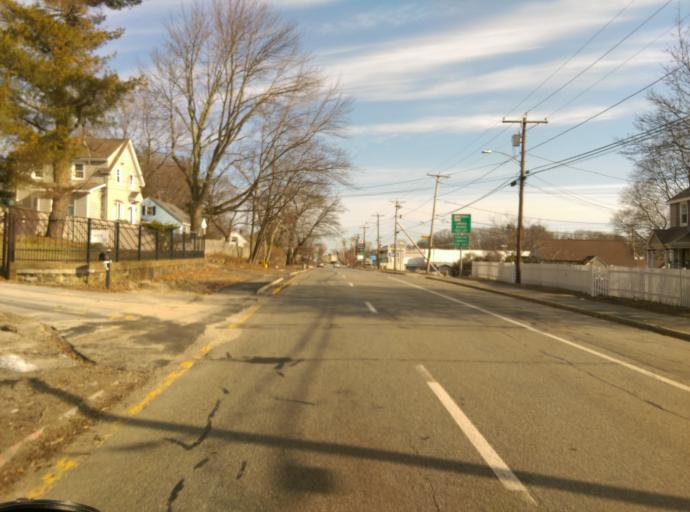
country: US
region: Massachusetts
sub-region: Essex County
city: North Andover
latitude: 42.6807
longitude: -71.1523
